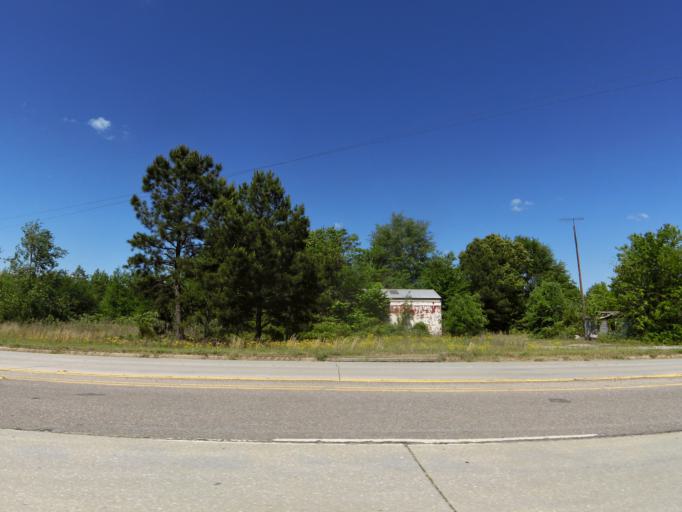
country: US
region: South Carolina
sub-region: Aiken County
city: Aiken
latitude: 33.5481
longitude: -81.6854
